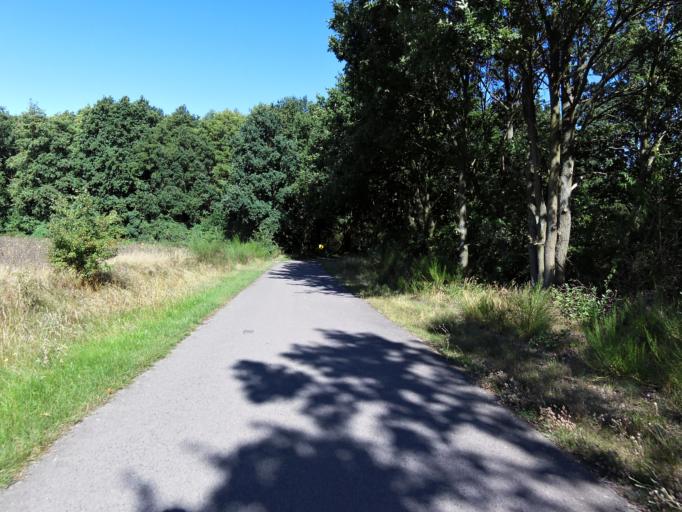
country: DE
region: Saxony-Anhalt
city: Pretzsch
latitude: 51.6738
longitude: 12.8258
